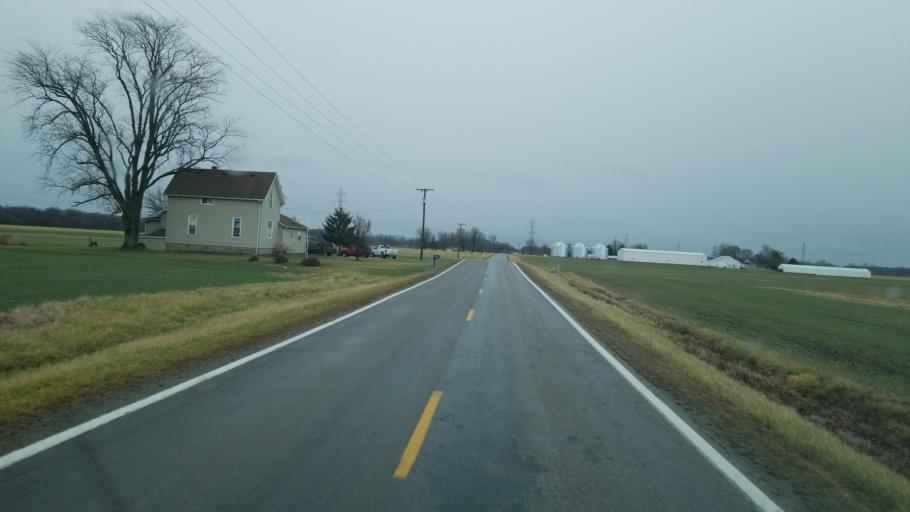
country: US
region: Ohio
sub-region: Union County
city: Richwood
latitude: 40.4040
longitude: -83.4319
